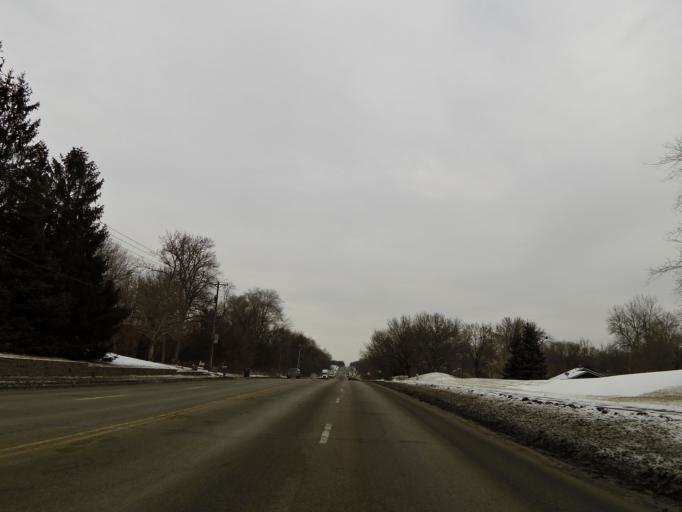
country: US
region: Minnesota
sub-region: Scott County
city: Savage
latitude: 44.8143
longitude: -93.3504
